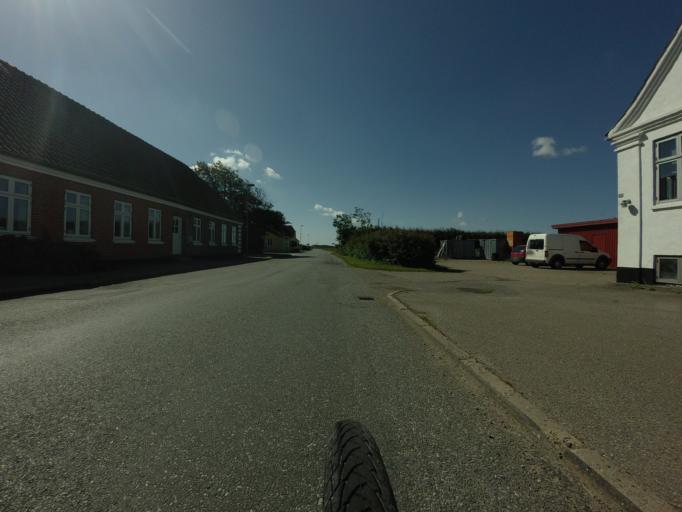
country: DK
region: North Denmark
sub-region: Hjorring Kommune
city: Hjorring
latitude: 57.4332
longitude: 9.9028
